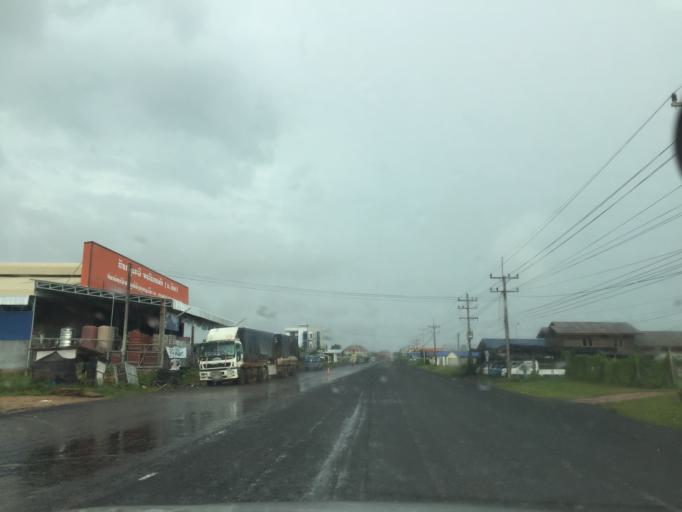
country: LA
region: Attapu
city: Attapu
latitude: 14.8255
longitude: 106.8081
